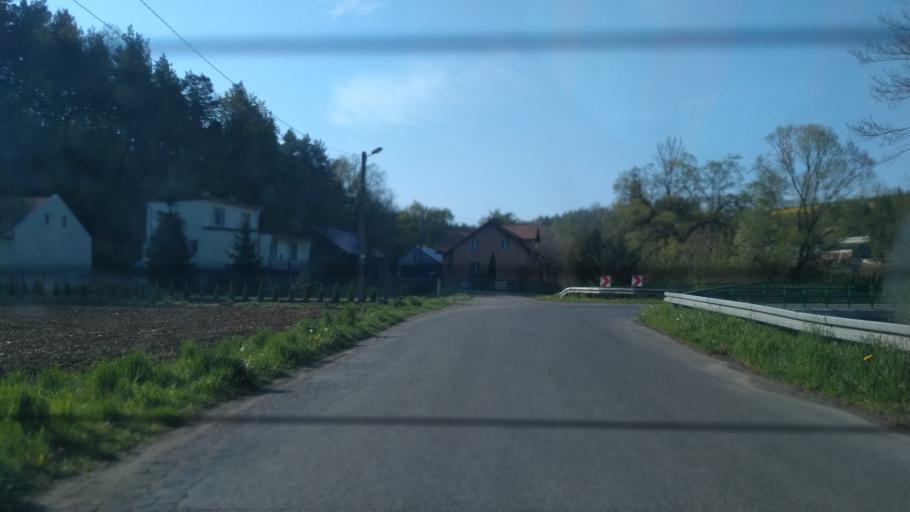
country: PL
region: Subcarpathian Voivodeship
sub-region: Powiat jaroslawski
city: Pruchnik
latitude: 49.8677
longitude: 22.5695
